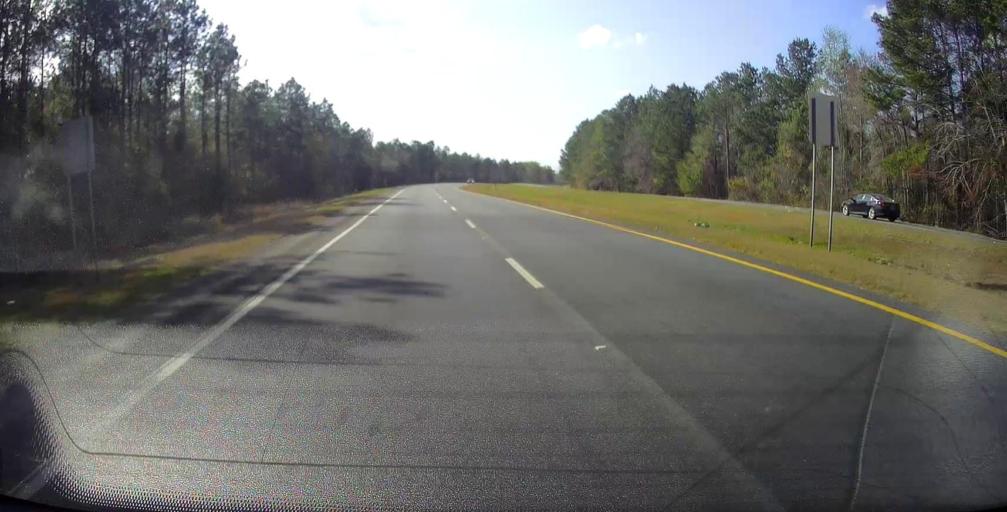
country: US
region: Georgia
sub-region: Dodge County
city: Eastman
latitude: 32.1084
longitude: -83.0889
